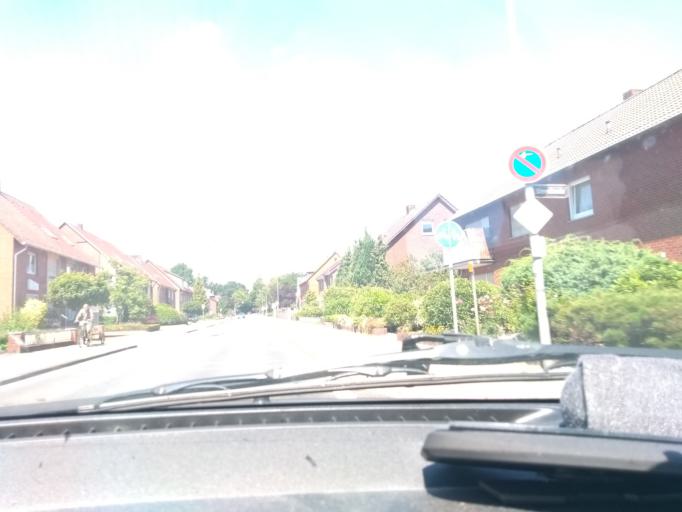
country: DE
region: Lower Saxony
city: Meppen
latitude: 52.6877
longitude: 7.3006
